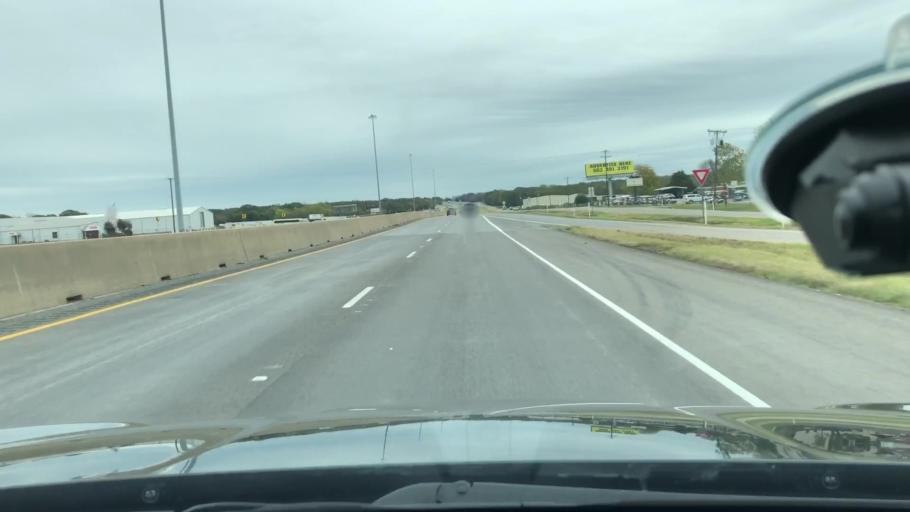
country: US
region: Texas
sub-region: Hunt County
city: Greenville
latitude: 33.1293
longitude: -95.9909
